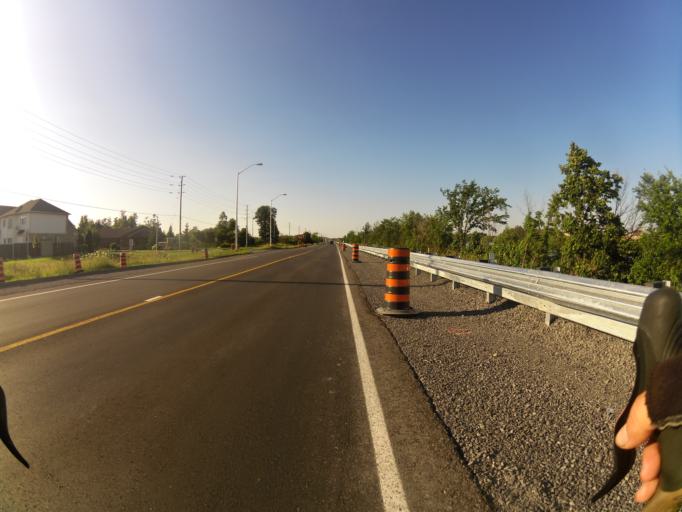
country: CA
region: Ontario
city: Bells Corners
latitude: 45.2754
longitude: -75.7039
